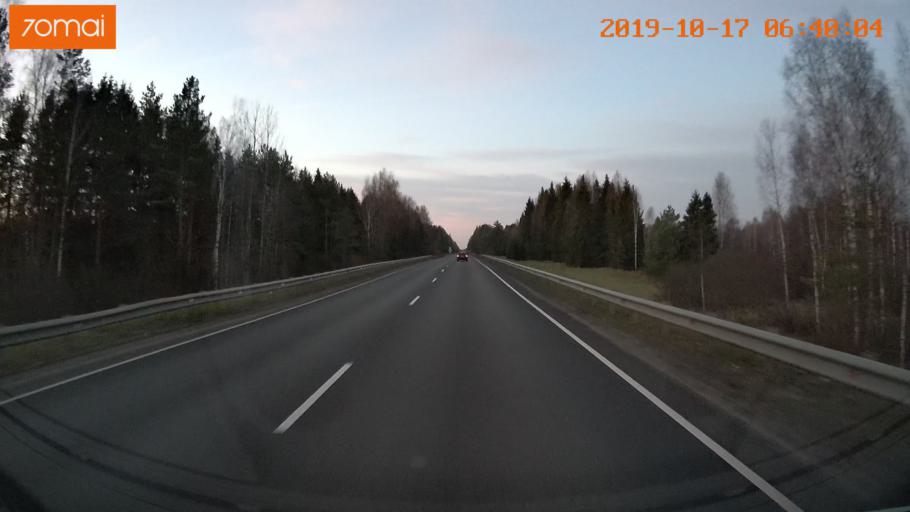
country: RU
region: Ivanovo
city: Novoye Leushino
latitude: 56.6344
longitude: 40.5731
